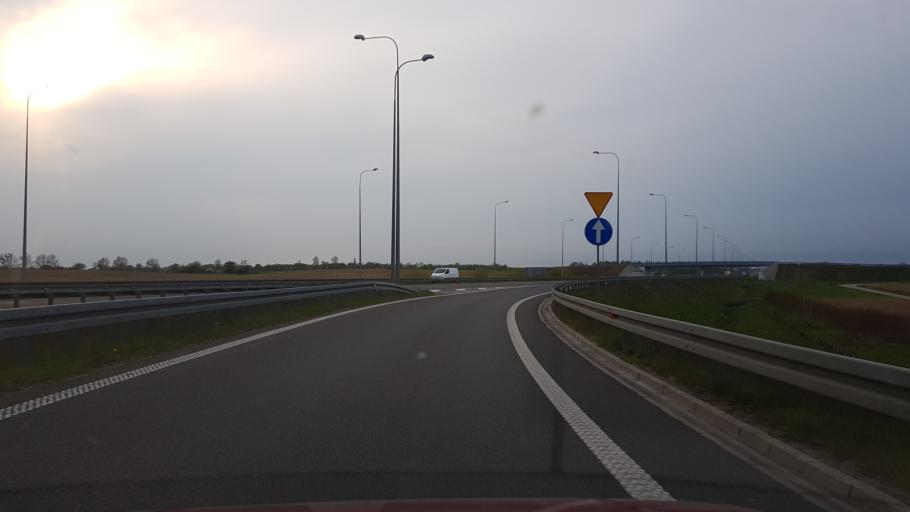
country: PL
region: West Pomeranian Voivodeship
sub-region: Powiat pyrzycki
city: Bielice
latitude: 53.2683
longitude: 14.6259
